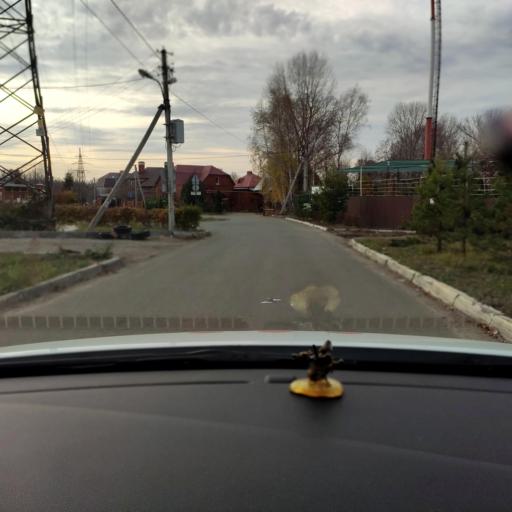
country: RU
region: Tatarstan
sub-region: Gorod Kazan'
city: Kazan
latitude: 55.7284
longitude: 49.1628
